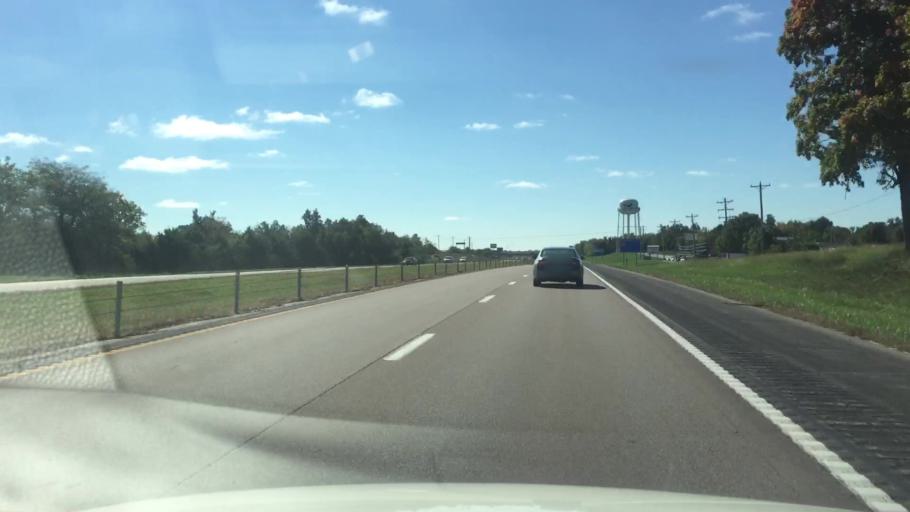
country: US
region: Missouri
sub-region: Boone County
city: Ashland
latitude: 38.7845
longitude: -92.2524
